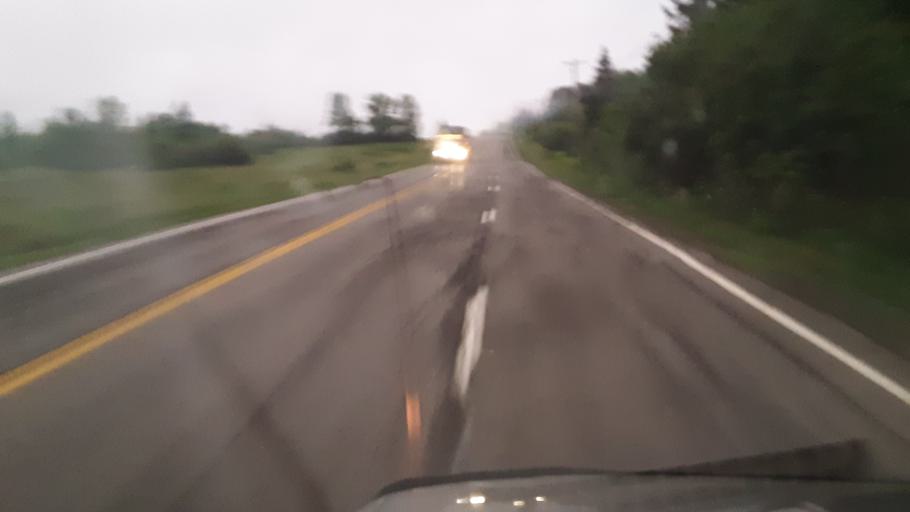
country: US
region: Maine
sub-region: Penobscot County
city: Patten
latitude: 46.0505
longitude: -68.4427
